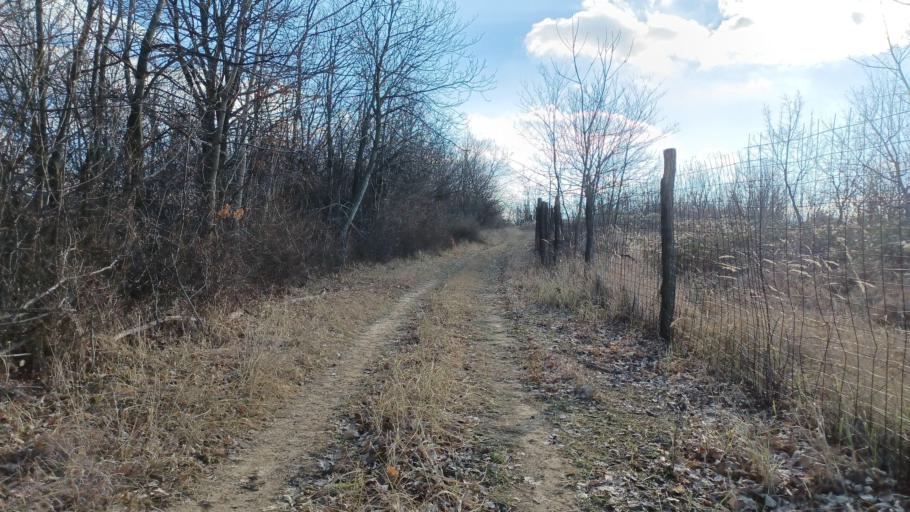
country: HU
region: Tolna
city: Szentgalpuszta
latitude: 46.3290
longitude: 18.6122
